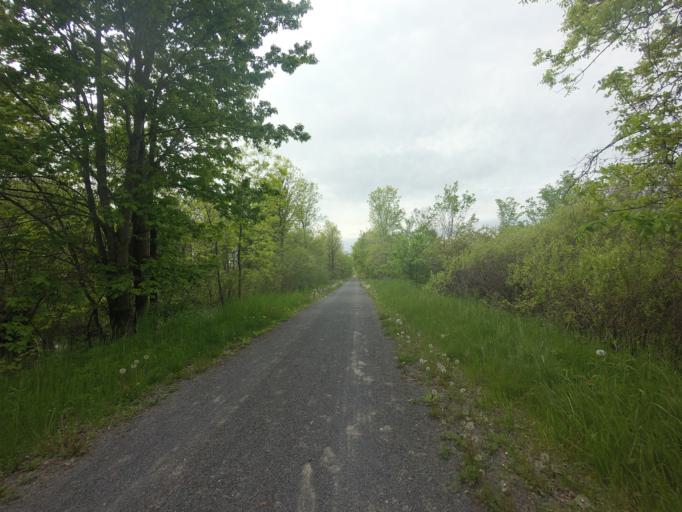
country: CA
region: Ontario
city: Kingston
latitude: 44.3474
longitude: -76.6090
